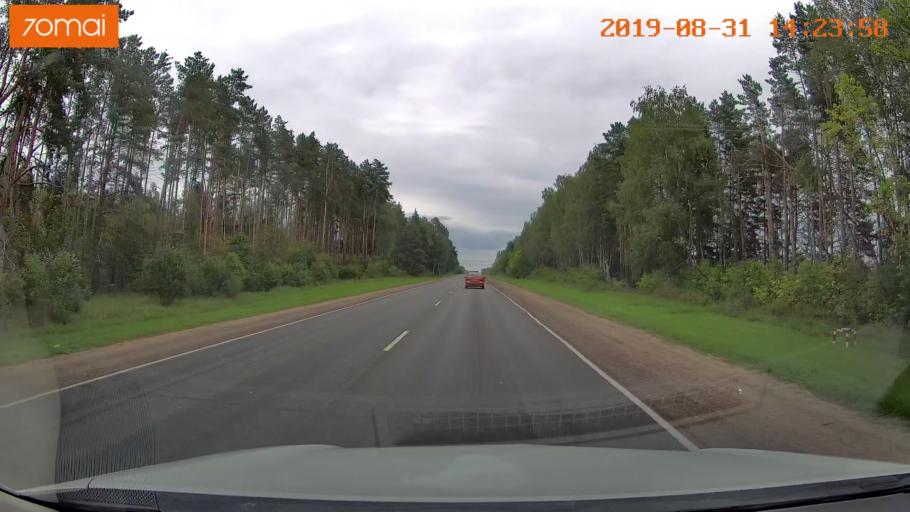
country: RU
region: Smolensk
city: Yekimovichi
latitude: 54.0999
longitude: 33.2454
